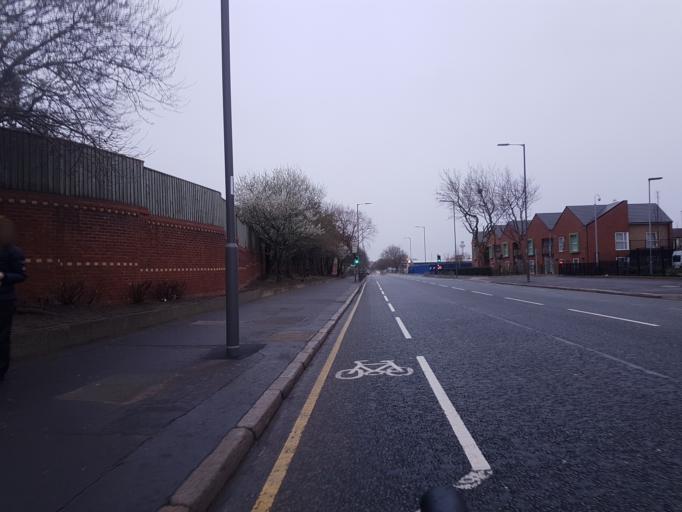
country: GB
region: England
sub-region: Liverpool
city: Liverpool
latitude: 53.4270
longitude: -2.9791
